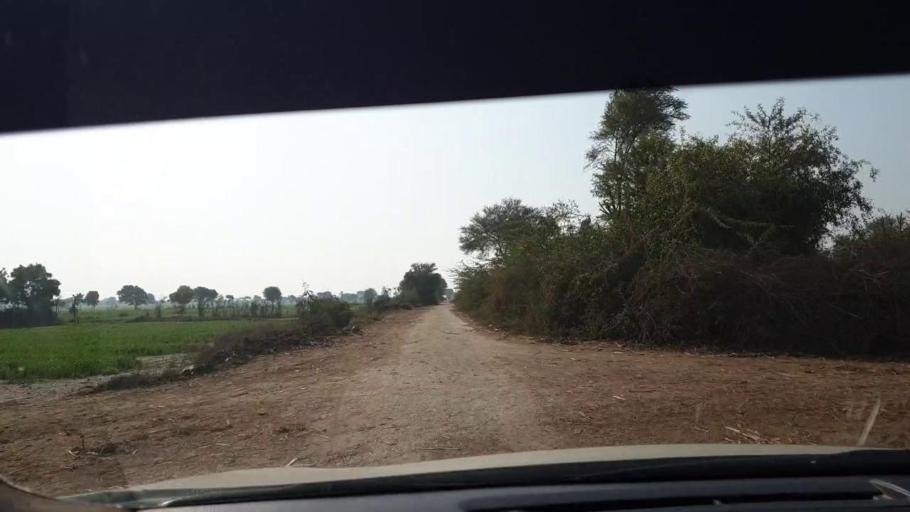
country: PK
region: Sindh
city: Tando Adam
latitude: 25.7688
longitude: 68.7246
